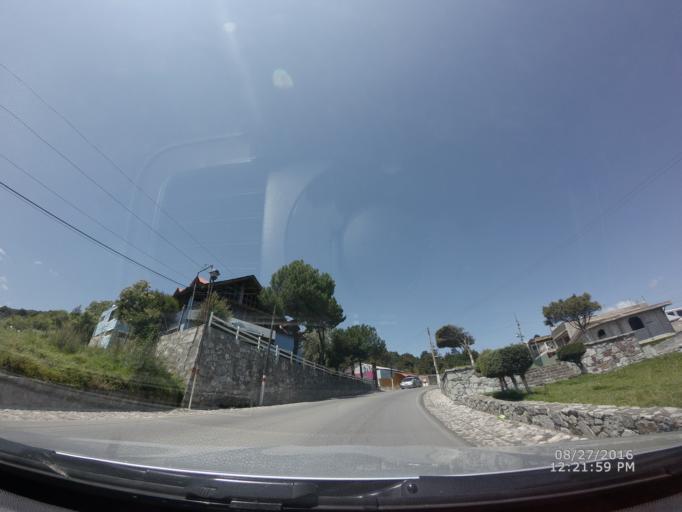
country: MX
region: Hidalgo
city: Mineral del Monte
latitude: 20.1359
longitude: -98.6798
